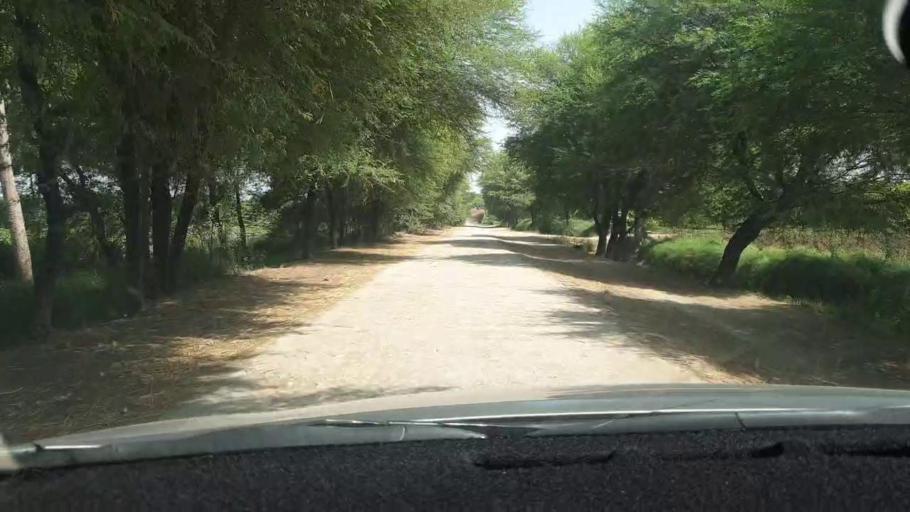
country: PK
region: Sindh
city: Tando Mittha Khan
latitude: 25.8453
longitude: 69.4487
